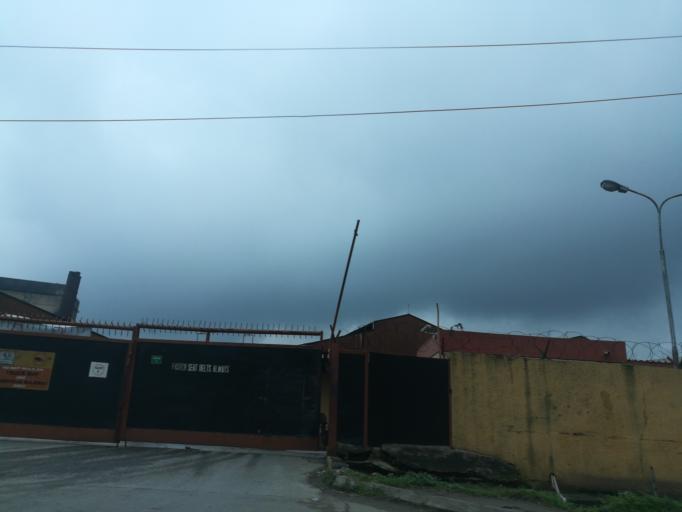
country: NG
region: Lagos
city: Agege
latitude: 6.6156
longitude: 3.3354
